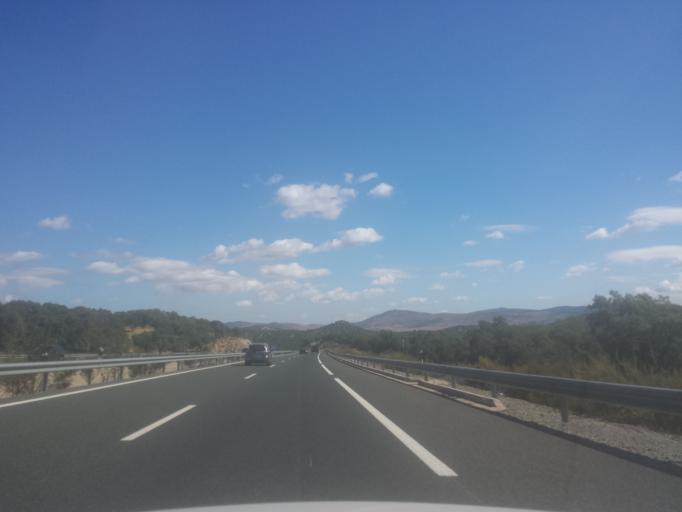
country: ES
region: Andalusia
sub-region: Provincia de Huelva
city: Santa Olalla del Cala
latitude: 37.9314
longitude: -6.2275
